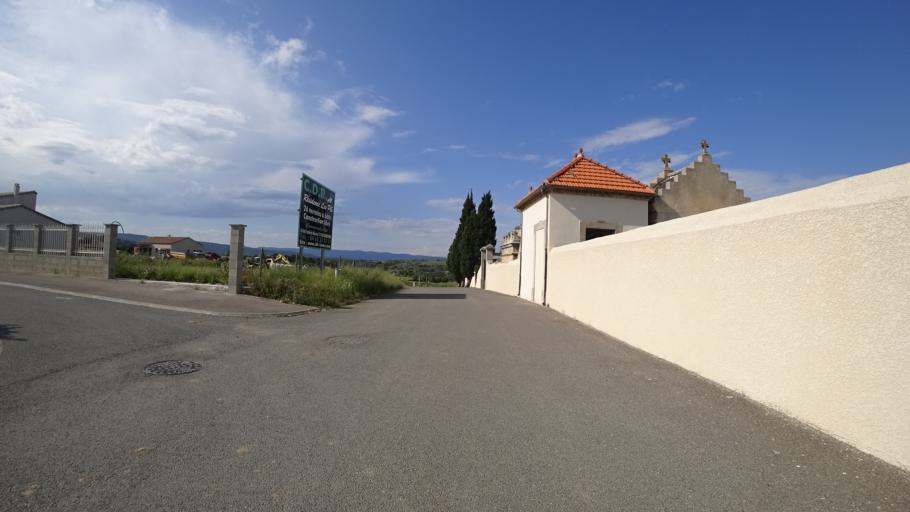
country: FR
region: Languedoc-Roussillon
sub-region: Departement de l'Aude
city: Canet
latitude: 43.2531
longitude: 2.8340
